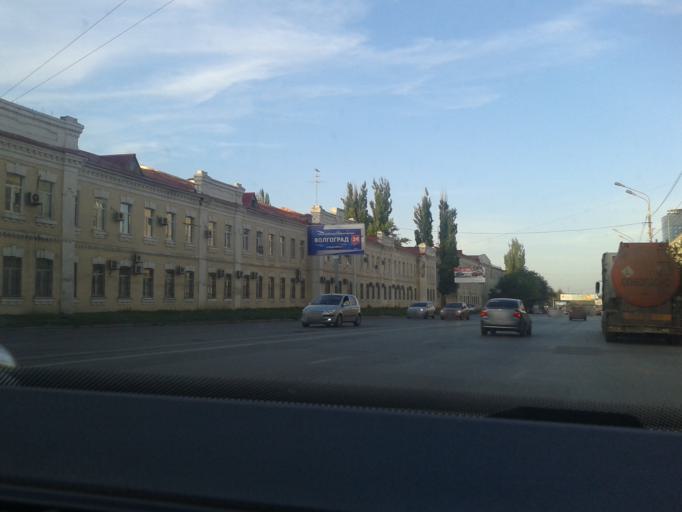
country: RU
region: Volgograd
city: Volgograd
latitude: 48.7259
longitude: 44.5171
